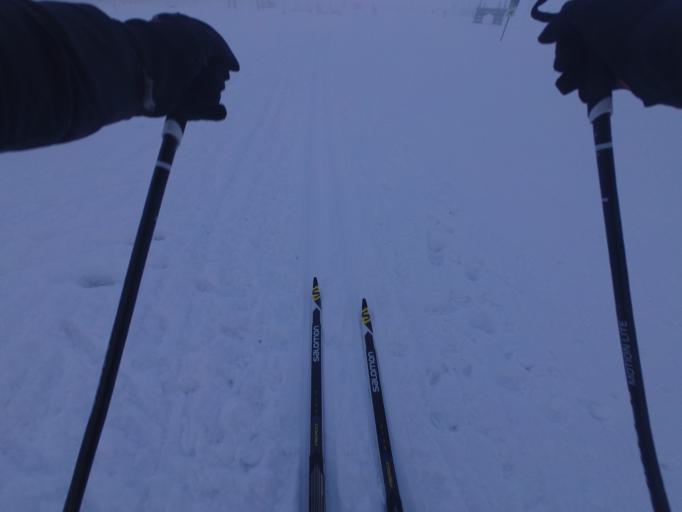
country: AT
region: Salzburg
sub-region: Politischer Bezirk Sankt Johann im Pongau
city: Wagrain
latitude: 47.3577
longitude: 13.3434
